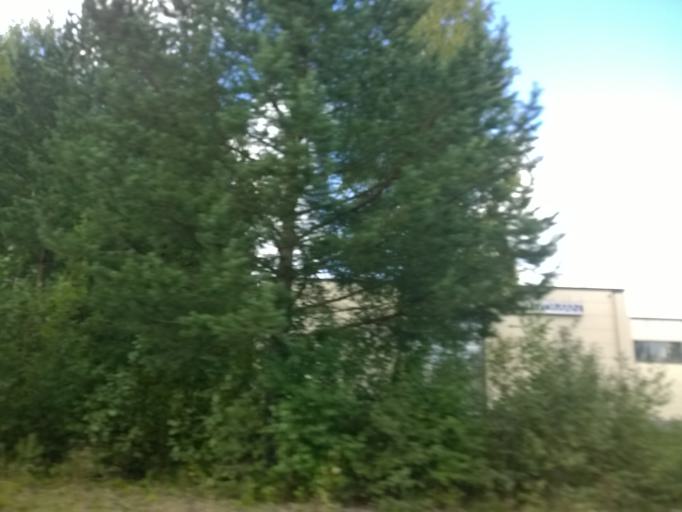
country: FI
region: Pirkanmaa
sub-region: Tampere
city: Tampere
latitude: 61.4532
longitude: 23.8837
